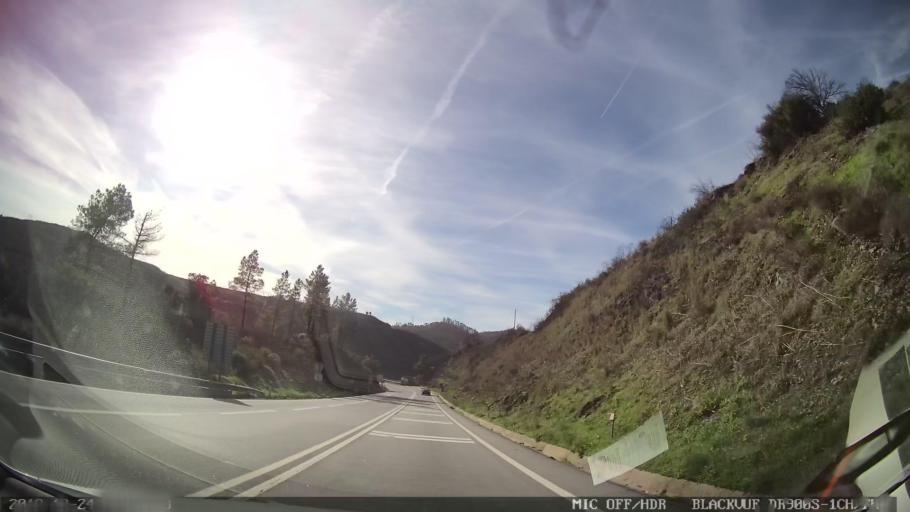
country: PT
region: Portalegre
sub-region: Gaviao
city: Gaviao
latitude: 39.5456
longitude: -7.8018
